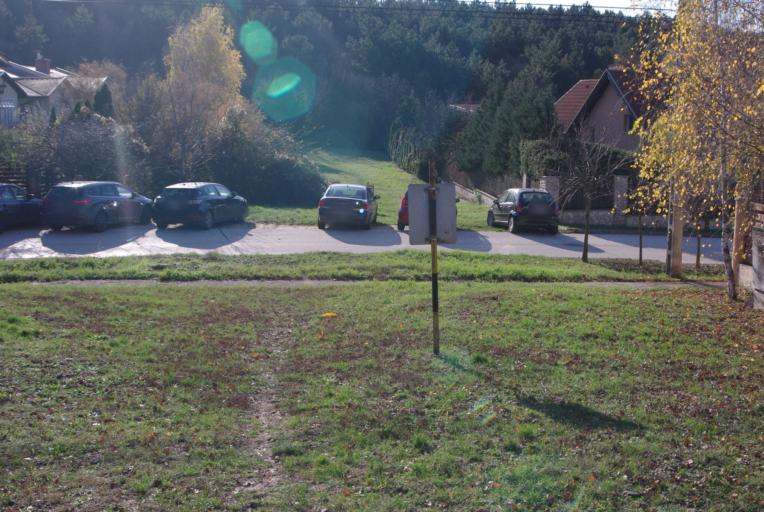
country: HU
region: Pest
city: Urom
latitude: 47.5901
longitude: 19.0265
